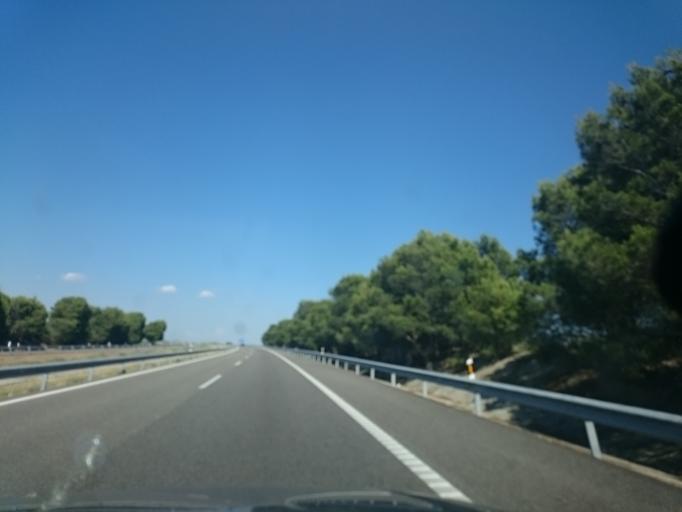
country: ES
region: Aragon
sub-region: Provincia de Zaragoza
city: Bujaraloz
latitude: 41.5185
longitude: -0.2164
